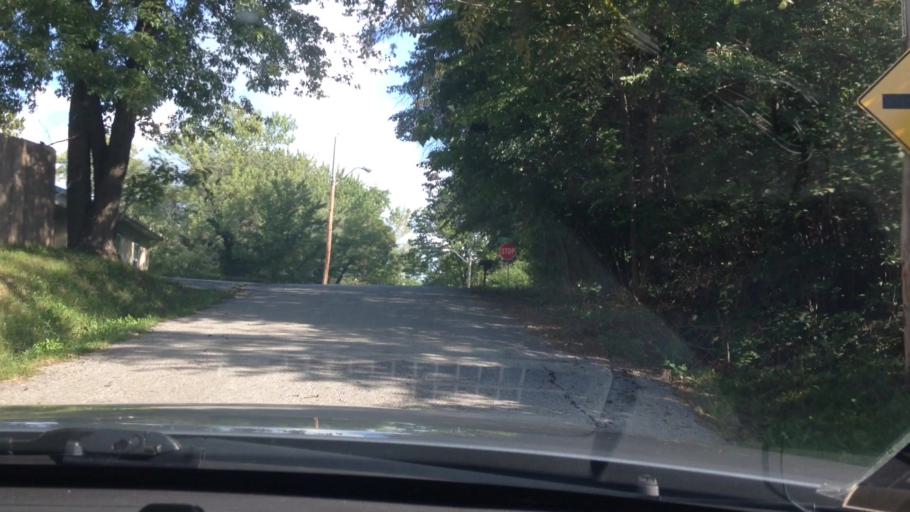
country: US
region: Missouri
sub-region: Clay County
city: Claycomo
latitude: 39.1885
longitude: -94.5120
